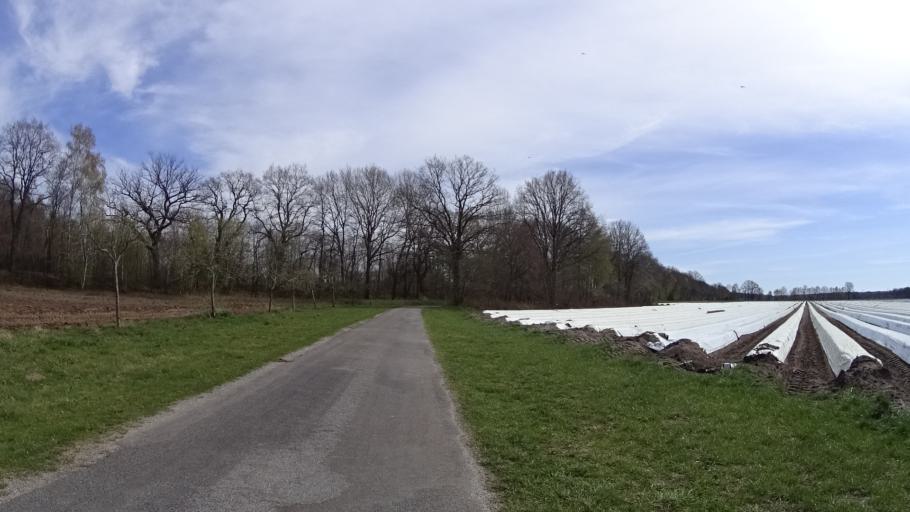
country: DE
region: Lower Saxony
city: Lunne
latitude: 52.4024
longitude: 7.3772
